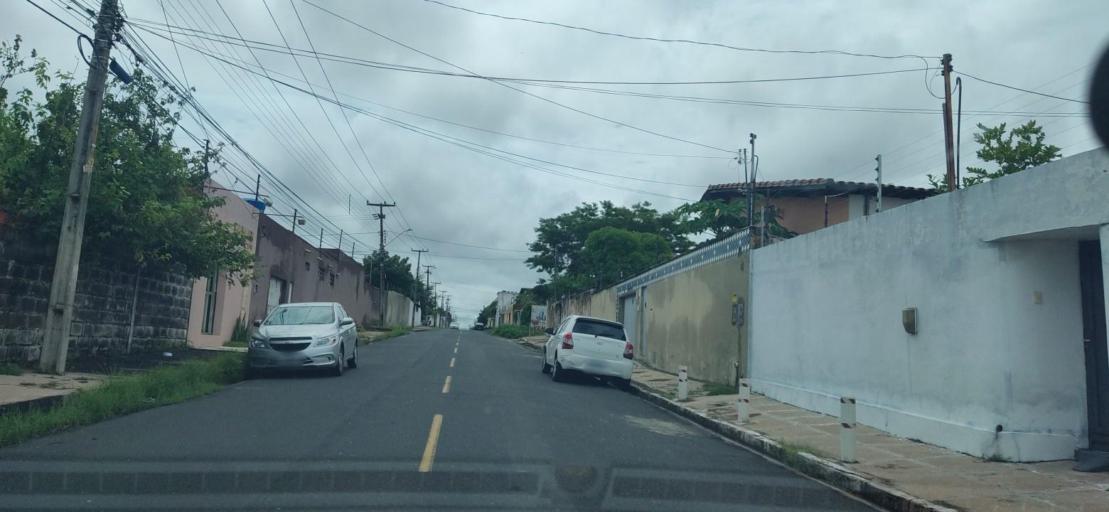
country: BR
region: Piaui
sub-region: Teresina
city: Teresina
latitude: -5.0715
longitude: -42.7660
